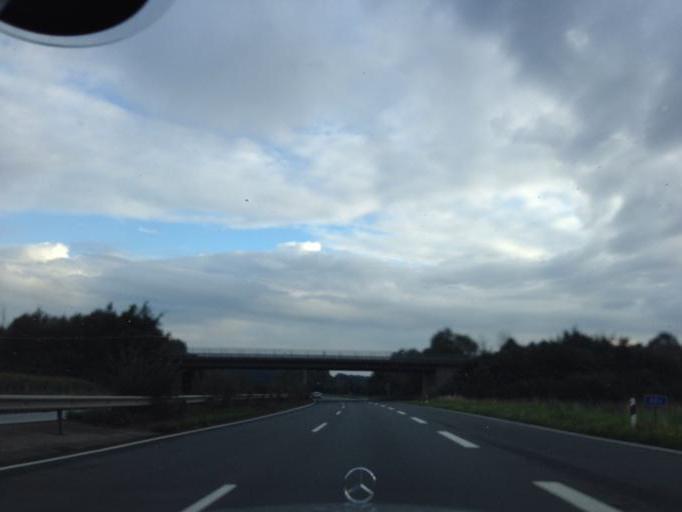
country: DE
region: Schleswig-Holstein
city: Rumpel
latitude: 53.8119
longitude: 10.3240
